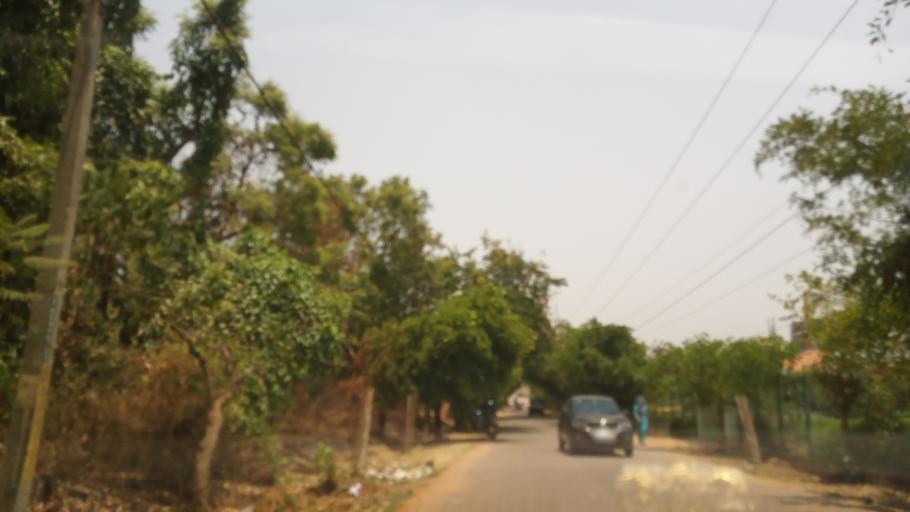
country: IN
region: Karnataka
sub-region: Bangalore Urban
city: Bangalore
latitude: 13.0375
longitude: 77.5021
